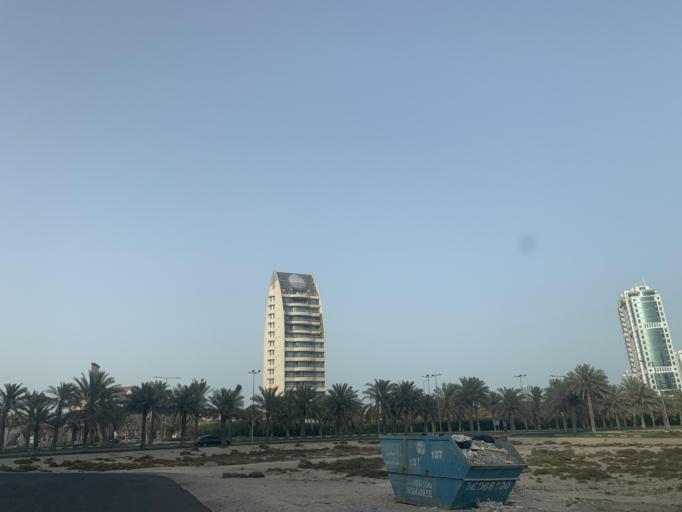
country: BH
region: Manama
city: Jidd Hafs
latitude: 26.2403
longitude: 50.5397
